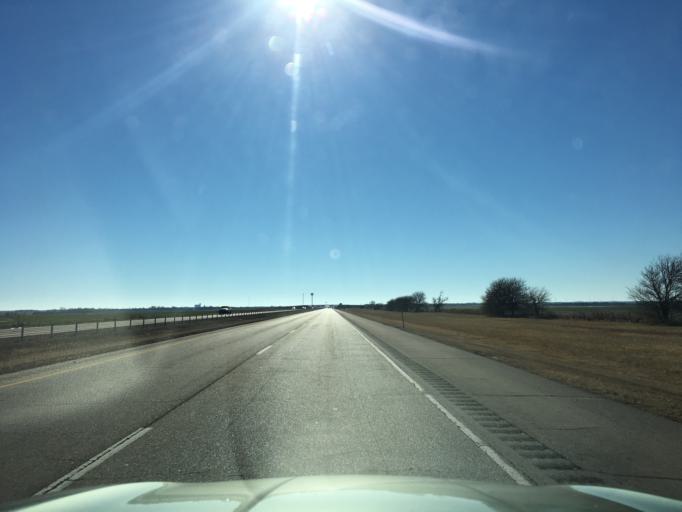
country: US
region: Oklahoma
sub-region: Kay County
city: Blackwell
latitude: 36.9651
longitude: -97.3458
